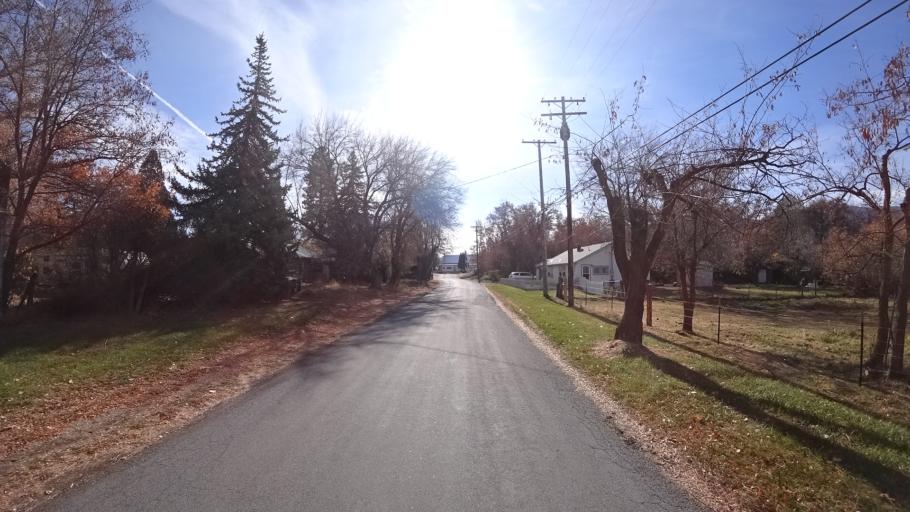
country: US
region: California
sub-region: Siskiyou County
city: Weed
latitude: 41.4593
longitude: -122.4328
